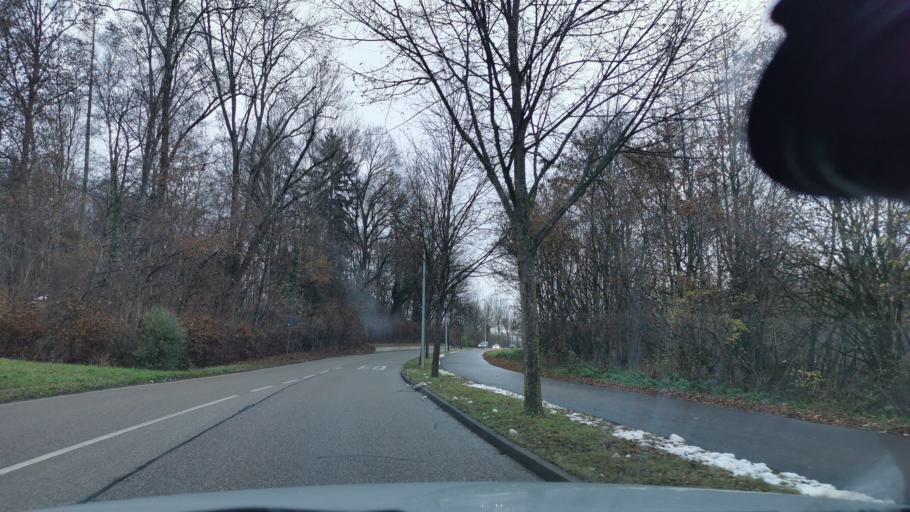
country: DE
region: Baden-Wuerttemberg
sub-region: Regierungsbezirk Stuttgart
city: Goeppingen
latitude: 48.7052
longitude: 9.6776
